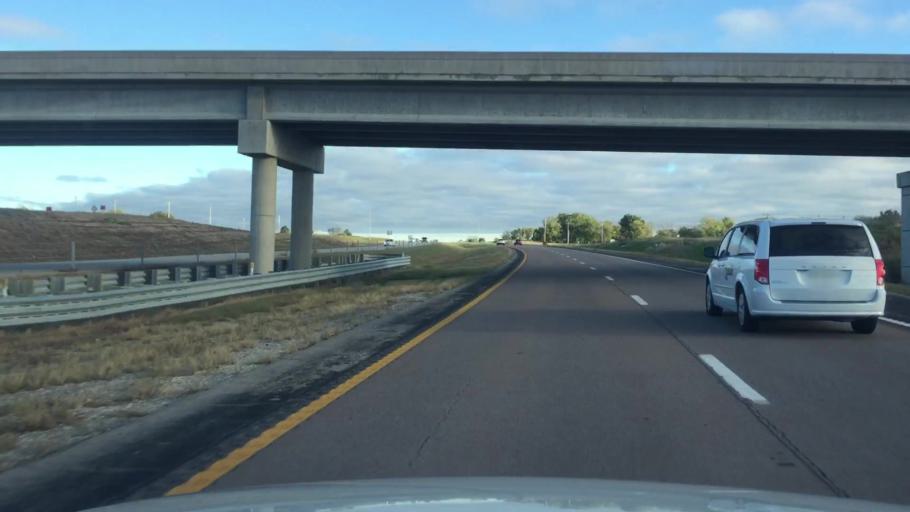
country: US
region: Missouri
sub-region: Boone County
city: Ashland
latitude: 38.8322
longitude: -92.2492
